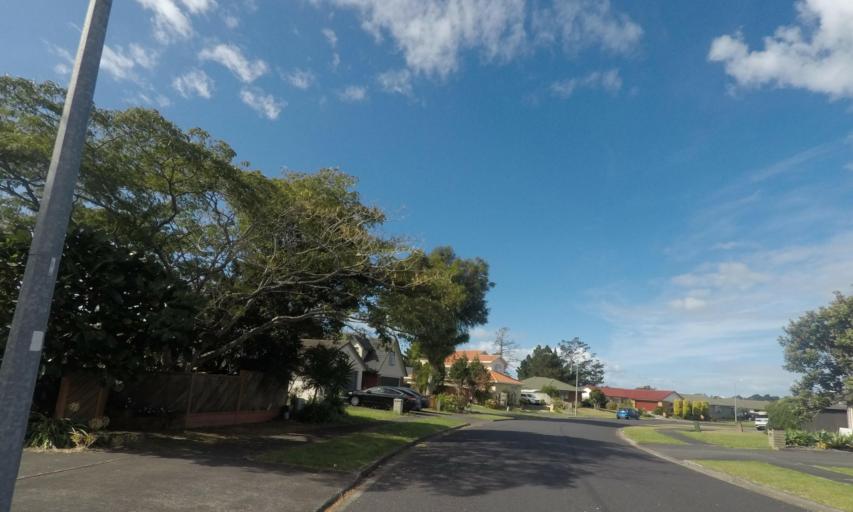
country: NZ
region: Auckland
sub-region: Auckland
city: Pakuranga
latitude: -36.9223
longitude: 174.8921
